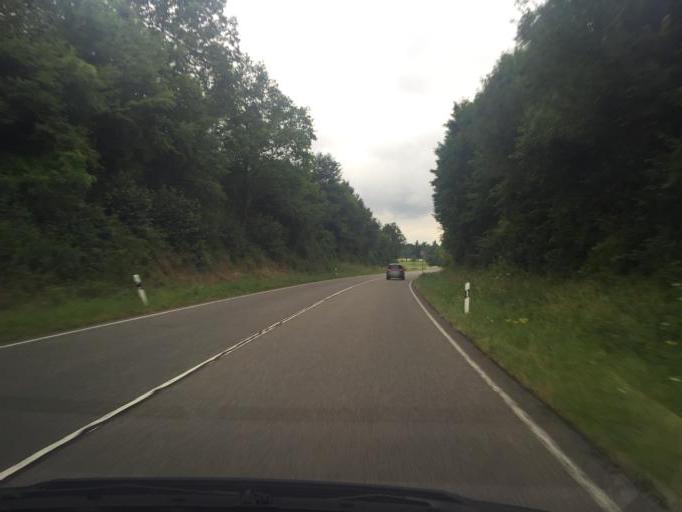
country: DE
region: Baden-Wuerttemberg
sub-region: Karlsruhe Region
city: Bretten
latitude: 48.9982
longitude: 8.7191
